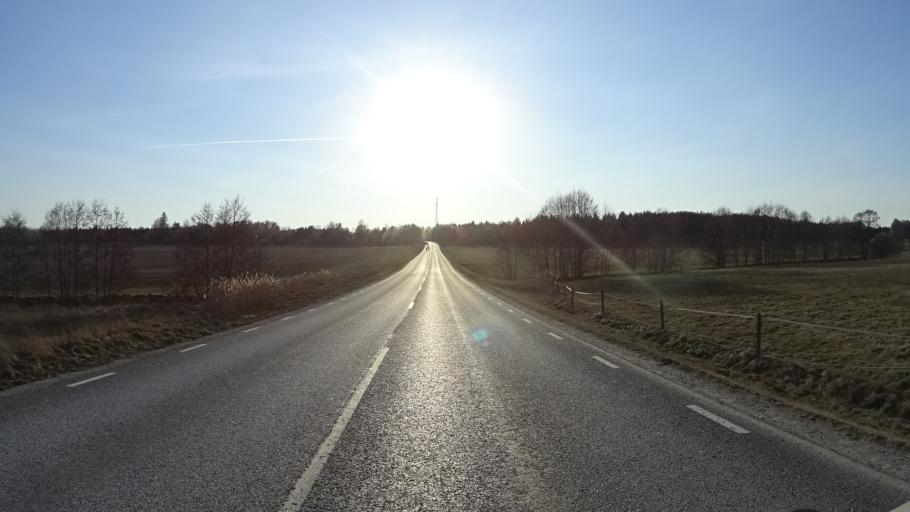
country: SE
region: Stockholm
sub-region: Osterakers Kommun
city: Akersberga
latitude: 59.4507
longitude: 18.2275
